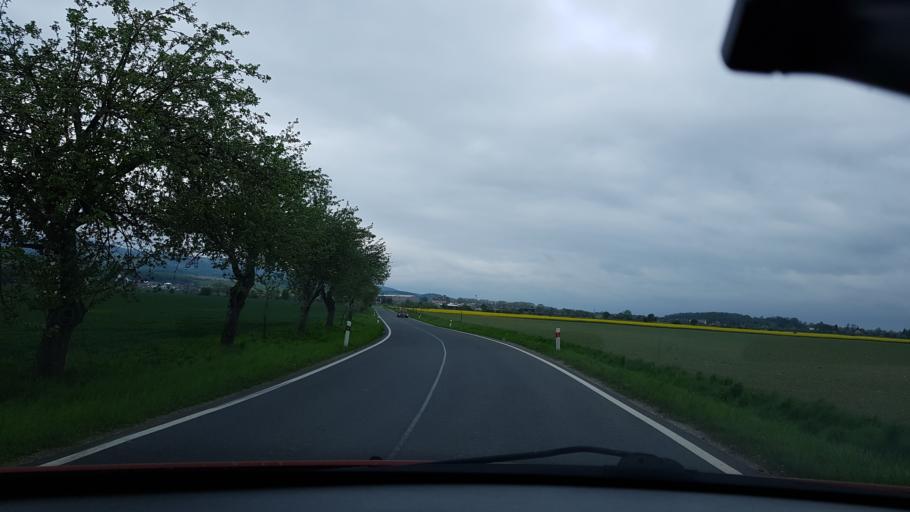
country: CZ
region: Olomoucky
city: Javornik
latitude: 50.3881
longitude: 17.0345
